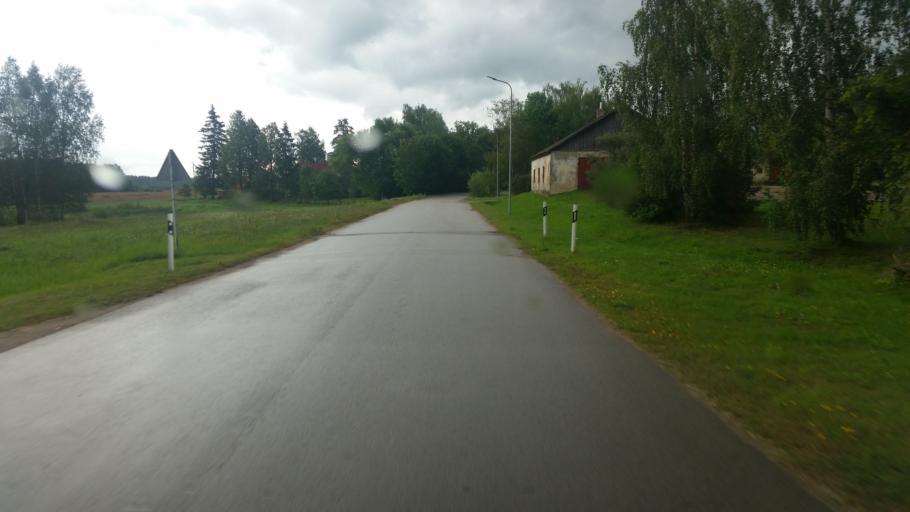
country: LV
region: Vecumnieki
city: Vecumnieki
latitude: 56.4323
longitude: 24.4659
